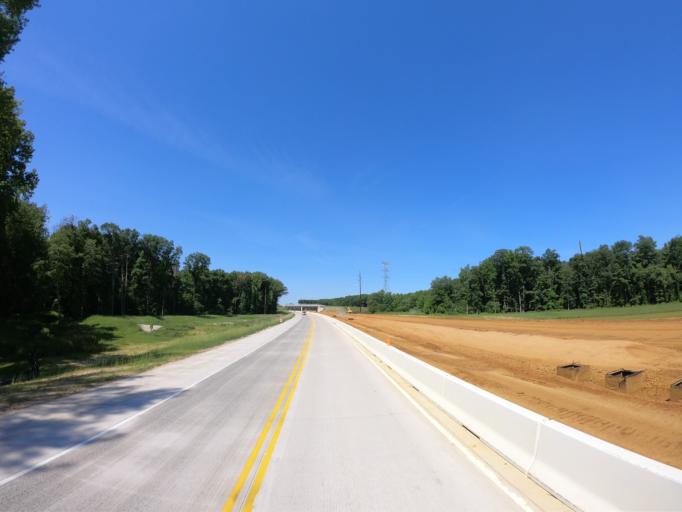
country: US
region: Delaware
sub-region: New Castle County
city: Middletown
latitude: 39.4124
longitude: -75.7692
